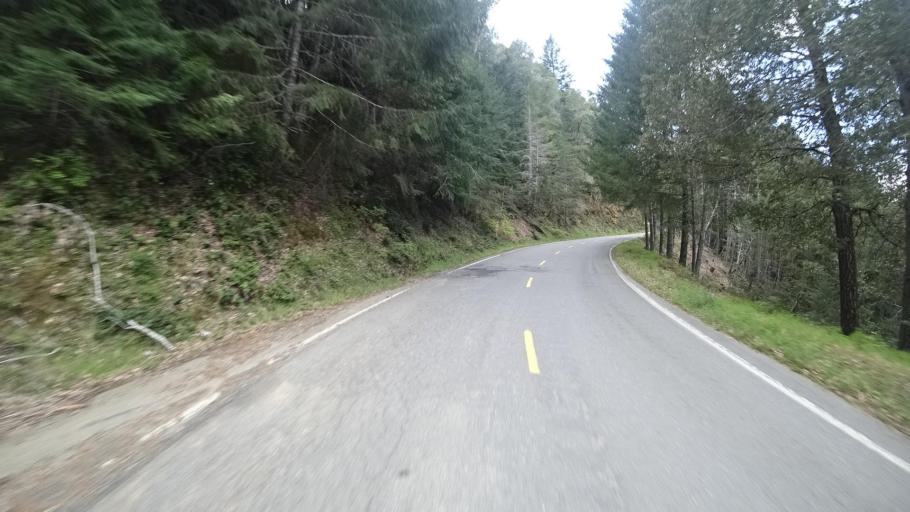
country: US
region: California
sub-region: Humboldt County
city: Redway
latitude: 40.0541
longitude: -123.9865
